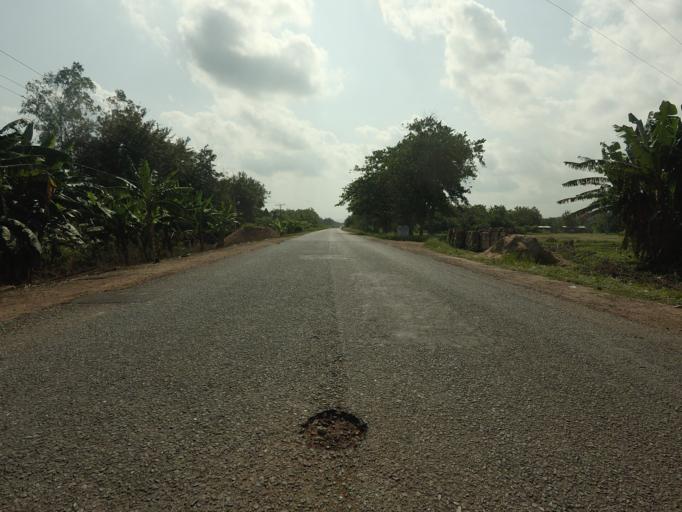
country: GH
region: Volta
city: Ho
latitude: 6.5770
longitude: 0.5858
